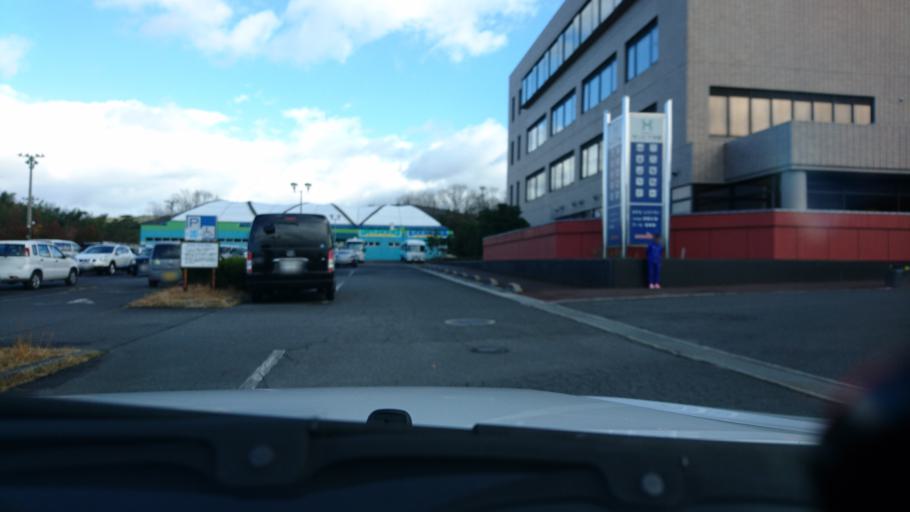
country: JP
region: Mie
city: Ueno-ebisumachi
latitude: 34.7562
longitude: 136.1571
